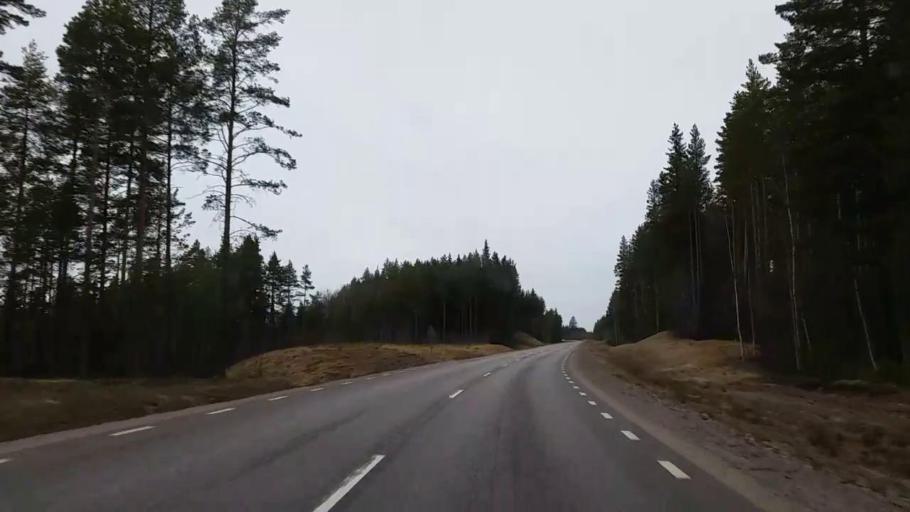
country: SE
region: Gaevleborg
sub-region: Ovanakers Kommun
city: Edsbyn
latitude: 61.1796
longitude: 15.8795
